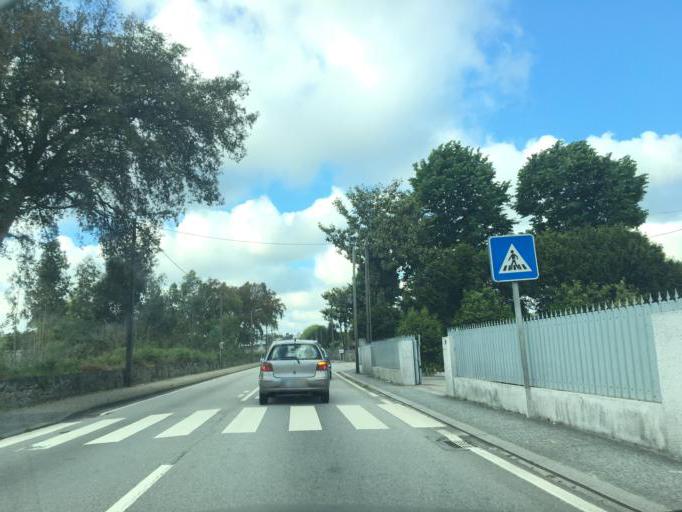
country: PT
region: Porto
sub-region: Maia
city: Anta
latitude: 41.2794
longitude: -8.6066
